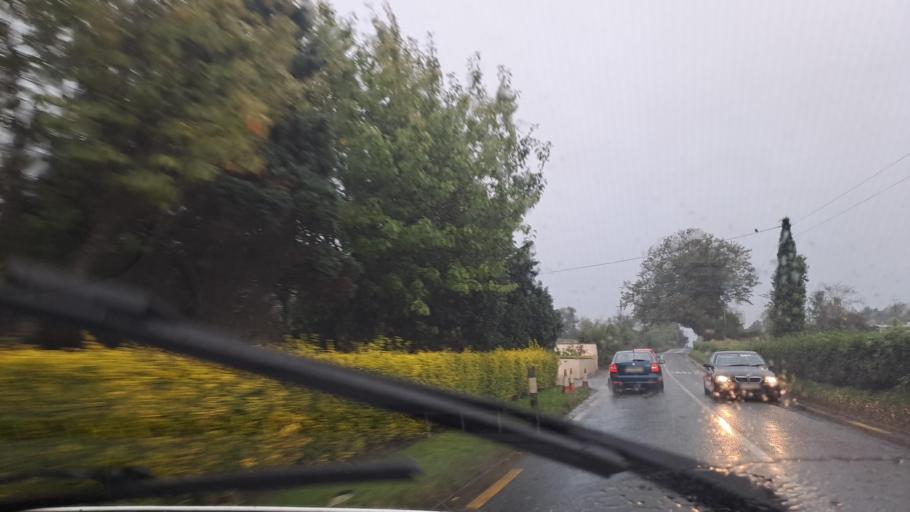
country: IE
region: Leinster
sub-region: Lu
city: Dundalk
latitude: 53.9778
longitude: -6.5244
